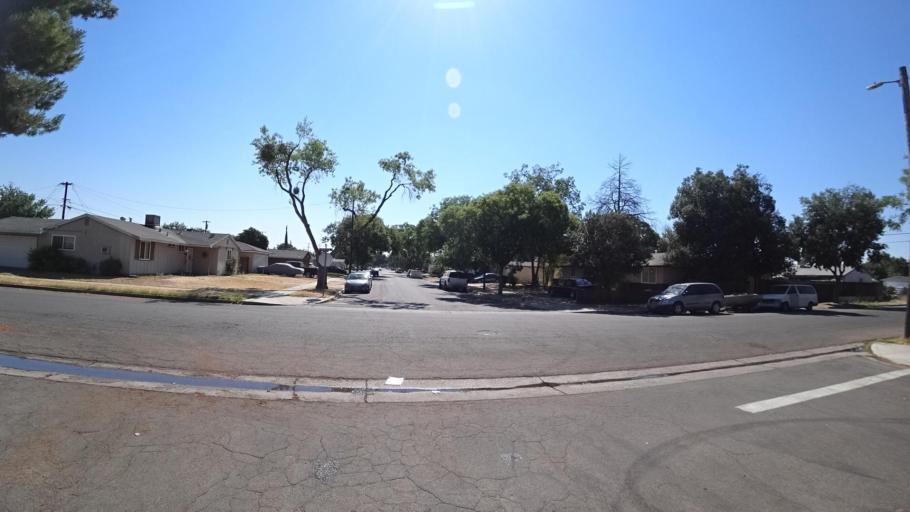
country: US
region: California
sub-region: Fresno County
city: Fresno
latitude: 36.7963
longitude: -119.7793
